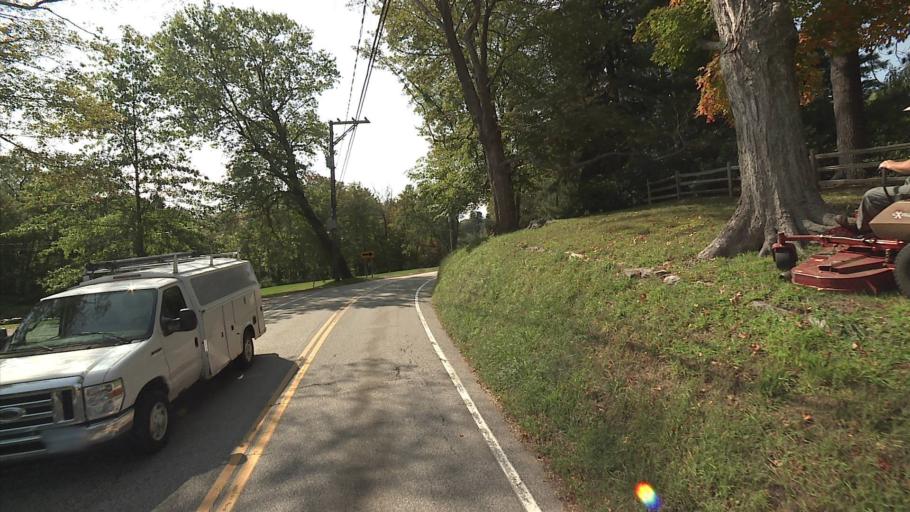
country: US
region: Connecticut
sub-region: Windham County
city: South Woodstock
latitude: 41.9051
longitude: -71.9584
